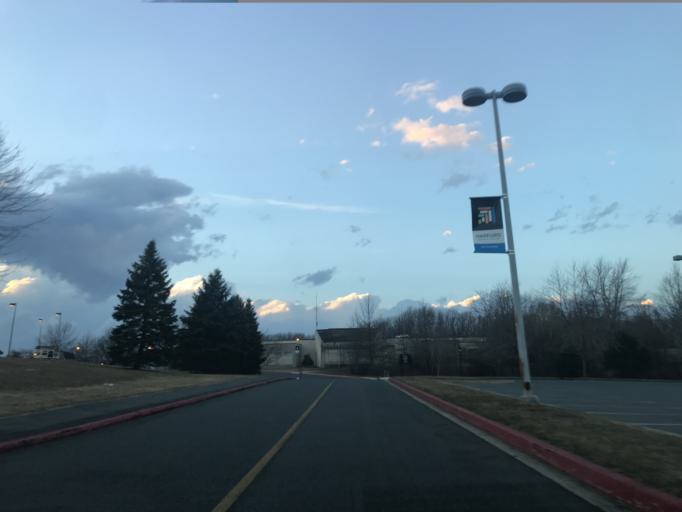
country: US
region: Maryland
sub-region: Harford County
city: South Bel Air
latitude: 39.5623
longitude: -76.2859
